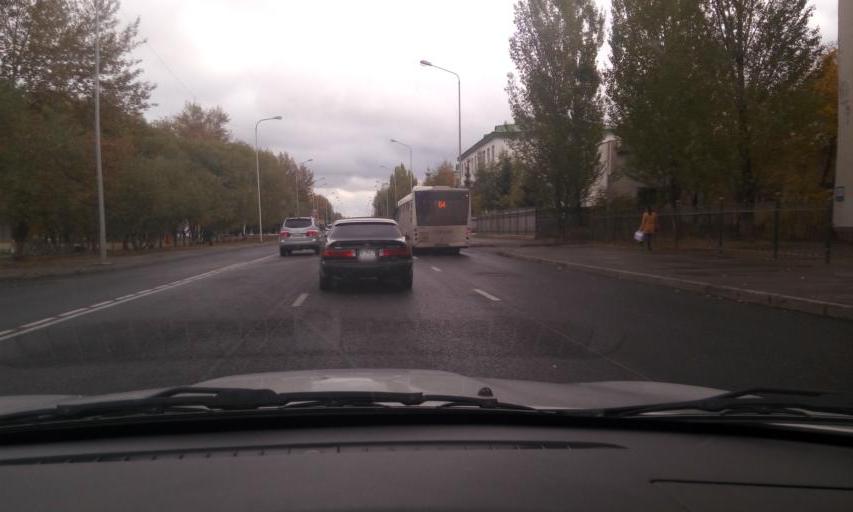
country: KZ
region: Astana Qalasy
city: Astana
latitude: 51.1698
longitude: 71.4516
